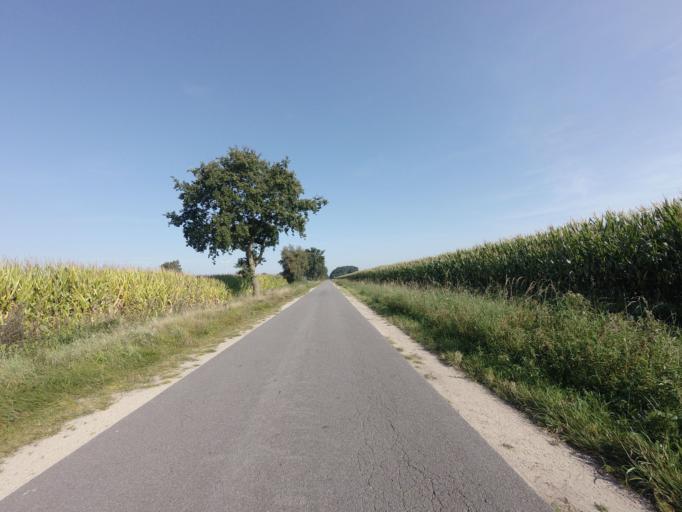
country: DE
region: Lower Saxony
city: Wielen
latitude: 52.5660
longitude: 6.7808
